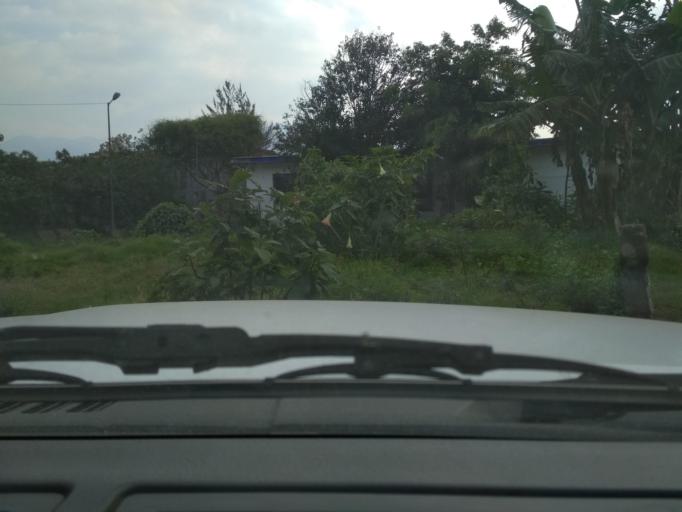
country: MX
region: Veracruz
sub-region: Mariano Escobedo
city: Palmira
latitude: 18.8722
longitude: -97.1004
